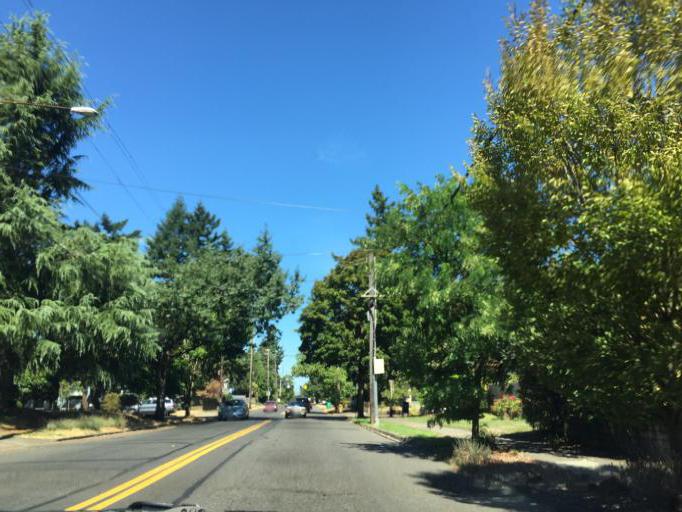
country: US
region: Oregon
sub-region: Multnomah County
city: Portland
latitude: 45.5512
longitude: -122.6306
